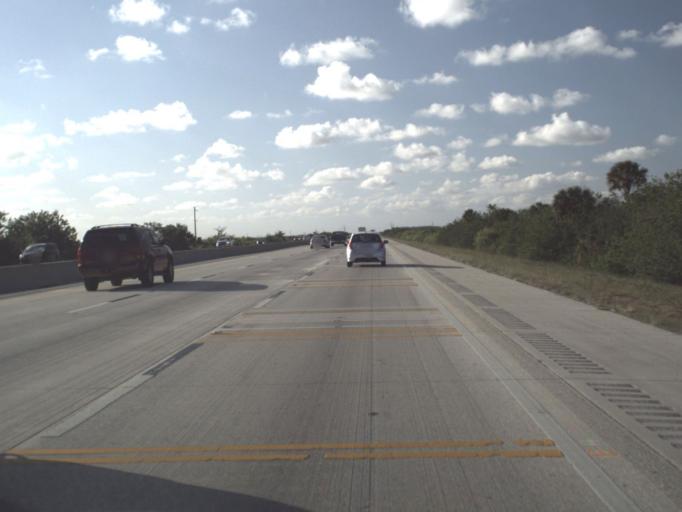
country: US
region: Florida
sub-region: Brevard County
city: Cocoa West
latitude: 28.3095
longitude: -80.7614
